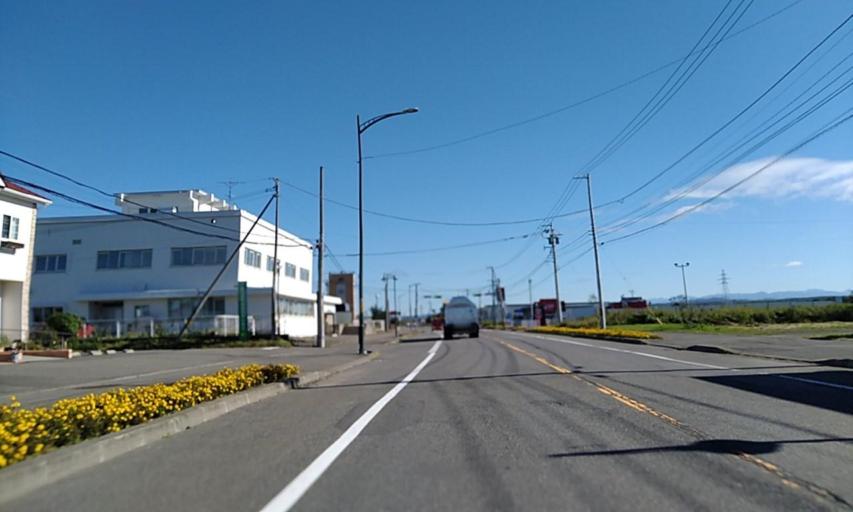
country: JP
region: Hokkaido
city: Shizunai-furukawacho
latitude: 42.5220
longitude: 142.0367
